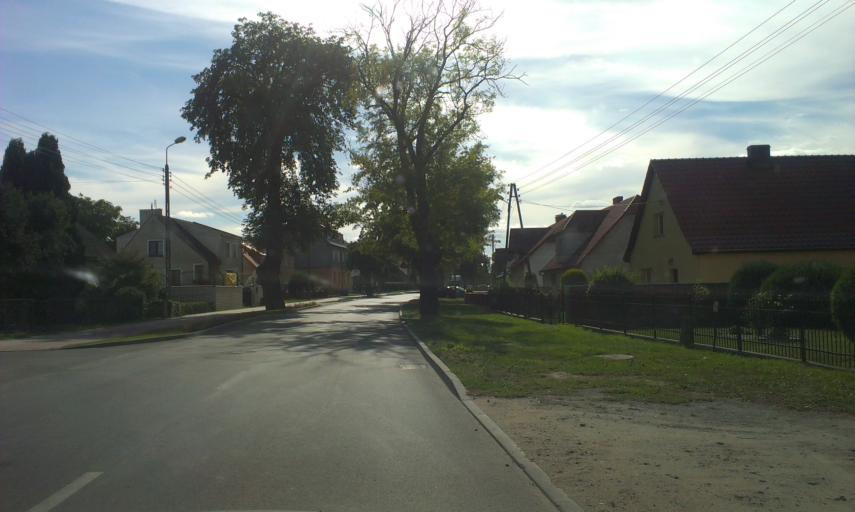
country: PL
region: Greater Poland Voivodeship
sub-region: Powiat pilski
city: Lobzenica
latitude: 53.2658
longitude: 17.2574
